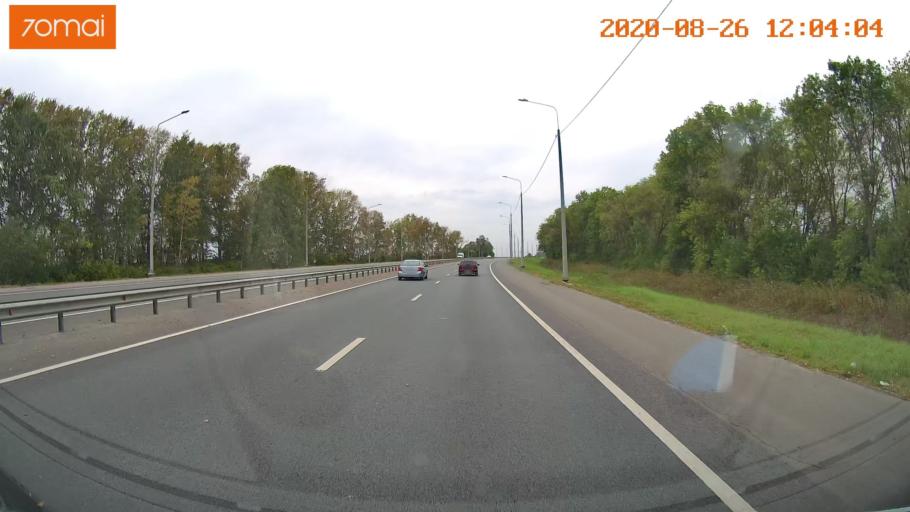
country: RU
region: Rjazan
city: Kiritsy
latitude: 54.3060
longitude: 40.1950
